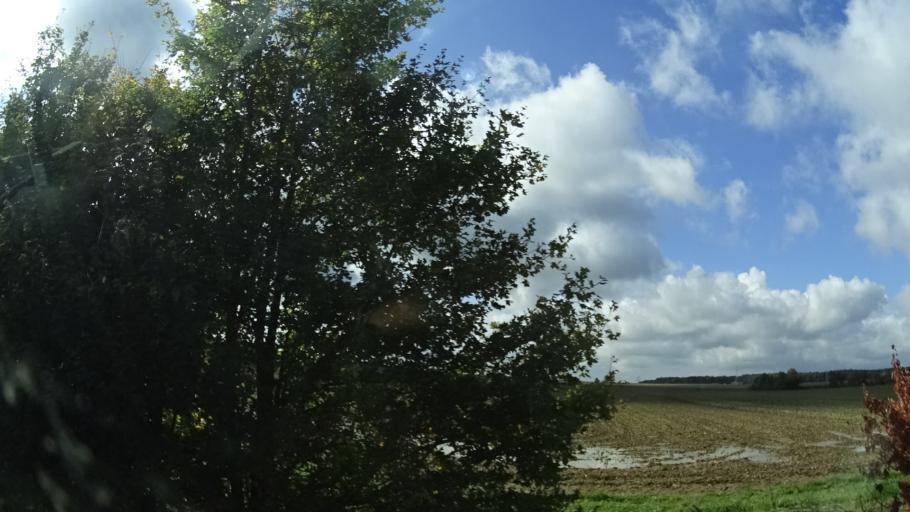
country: DE
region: Bavaria
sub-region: Regierungsbezirk Unterfranken
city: Biebelried
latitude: 49.7215
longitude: 10.0829
